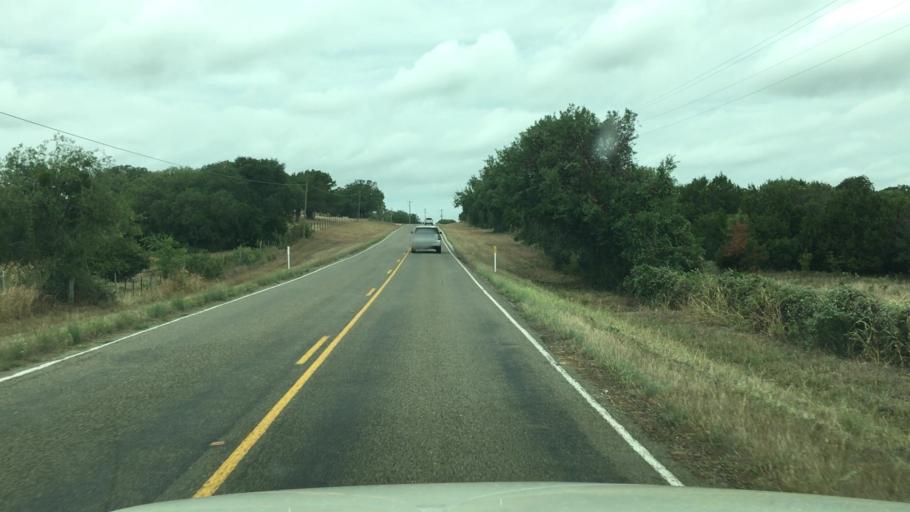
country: US
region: Texas
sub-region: Llano County
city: Horseshoe Bay
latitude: 30.4636
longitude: -98.4073
